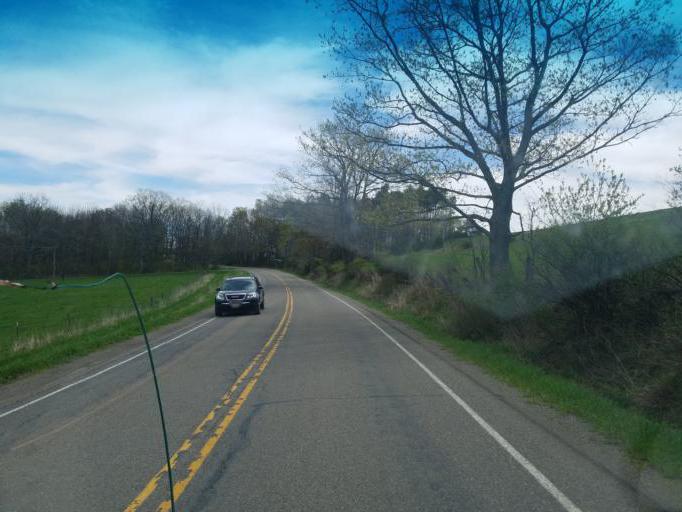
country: US
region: Pennsylvania
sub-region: Tioga County
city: Wellsboro
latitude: 41.7300
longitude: -77.3956
